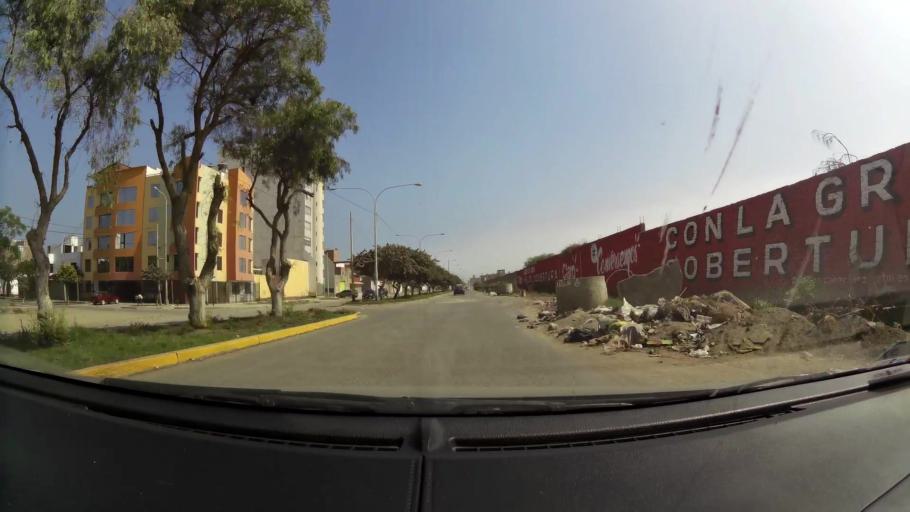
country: PE
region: La Libertad
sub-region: Provincia de Trujillo
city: Buenos Aires
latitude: -8.1280
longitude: -79.0479
